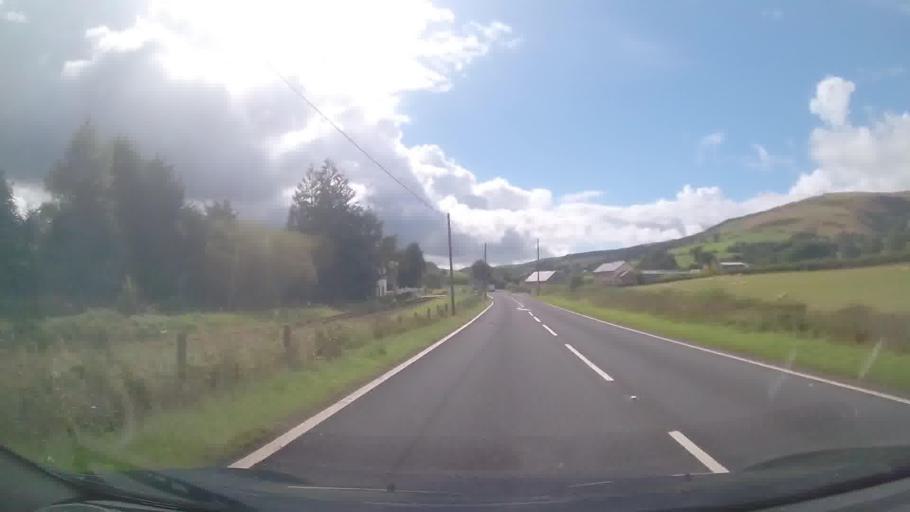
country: GB
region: Wales
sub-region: Carmarthenshire
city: Llandovery
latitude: 52.0925
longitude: -3.6617
